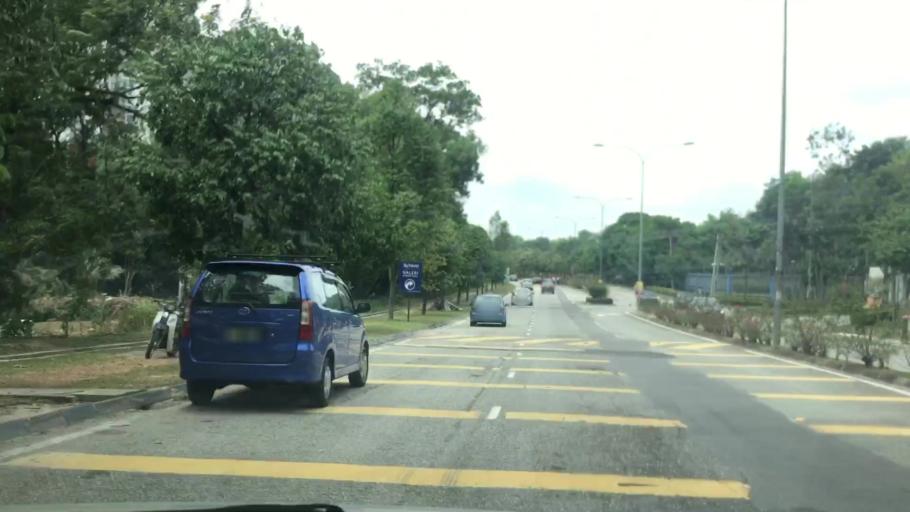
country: MY
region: Selangor
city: Kampong Baharu Balakong
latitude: 3.0542
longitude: 101.6765
